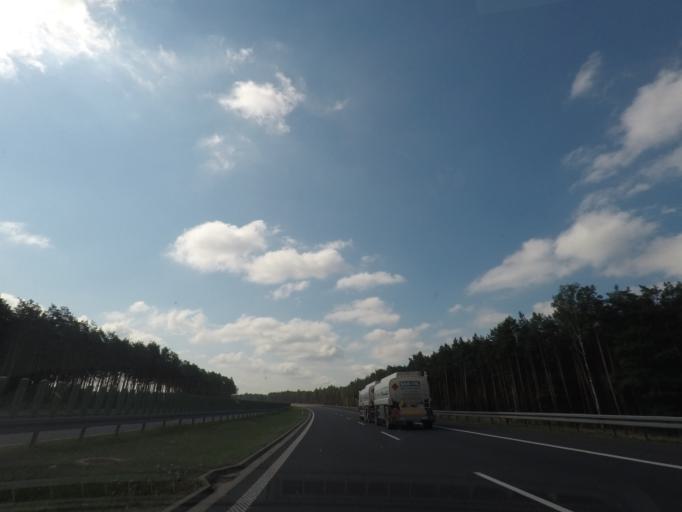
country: PL
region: Kujawsko-Pomorskie
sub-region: Powiat swiecki
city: Warlubie
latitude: 53.5277
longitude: 18.5995
